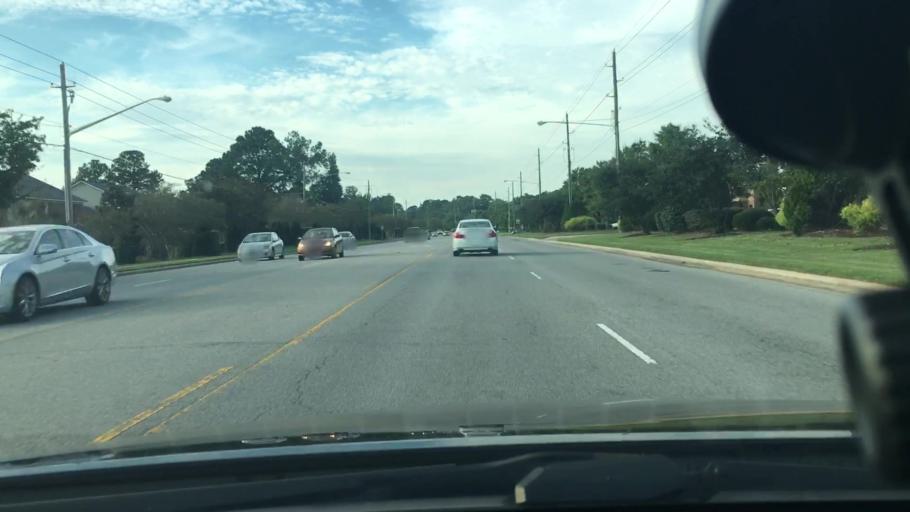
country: US
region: North Carolina
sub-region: Pitt County
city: Windsor
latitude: 35.5761
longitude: -77.3548
